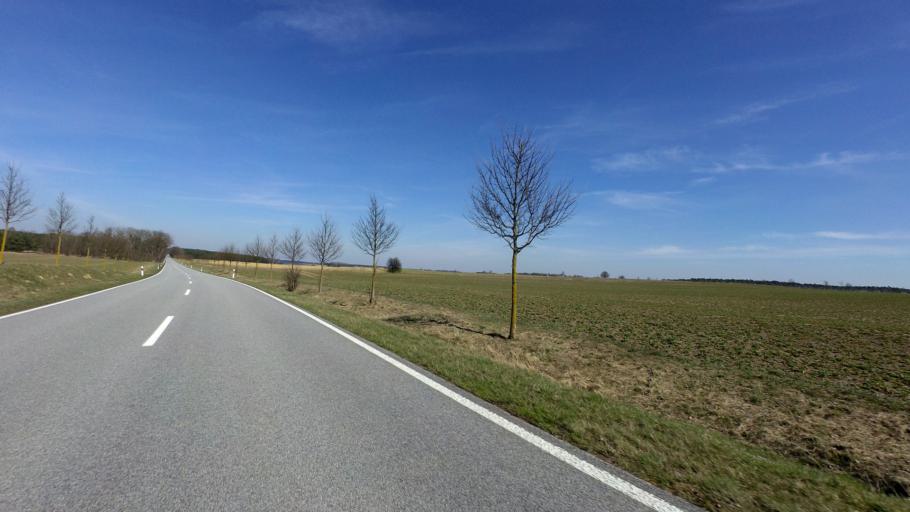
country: DE
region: Brandenburg
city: Waldsieversdorf
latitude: 52.4680
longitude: 14.0553
